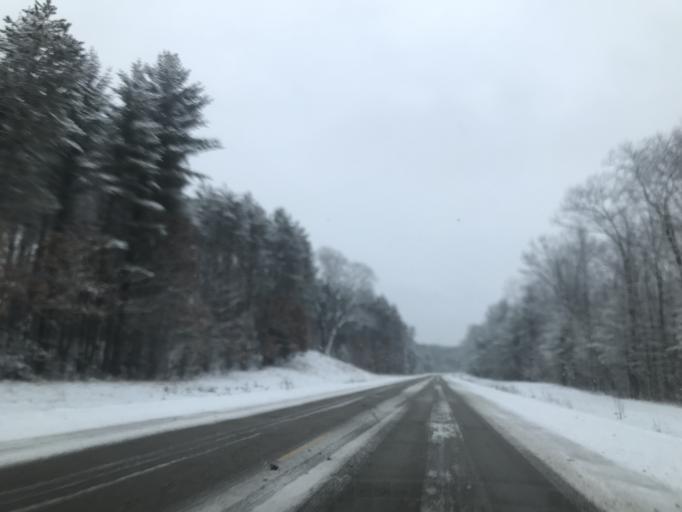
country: US
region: Wisconsin
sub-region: Oconto County
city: Oconto Falls
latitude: 44.8617
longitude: -88.0974
